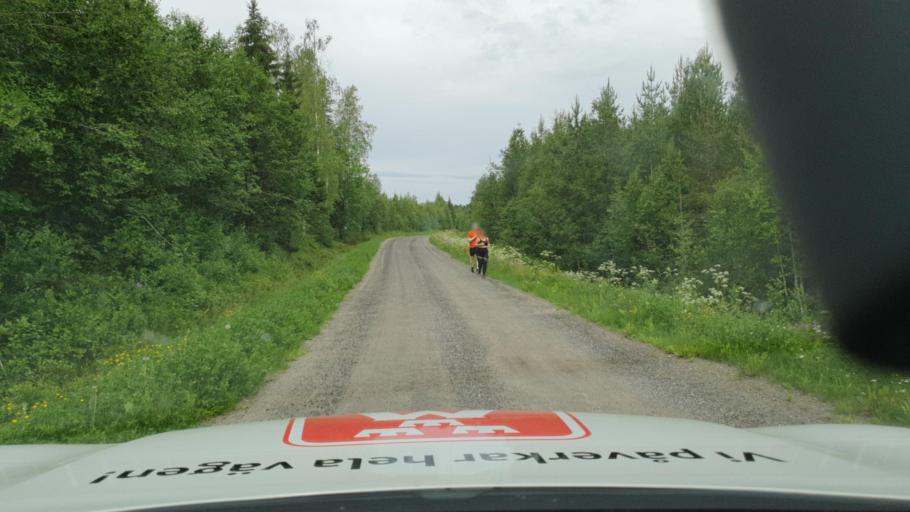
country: SE
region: Vaesterbotten
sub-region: Robertsfors Kommun
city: Robertsfors
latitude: 64.1954
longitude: 20.7122
